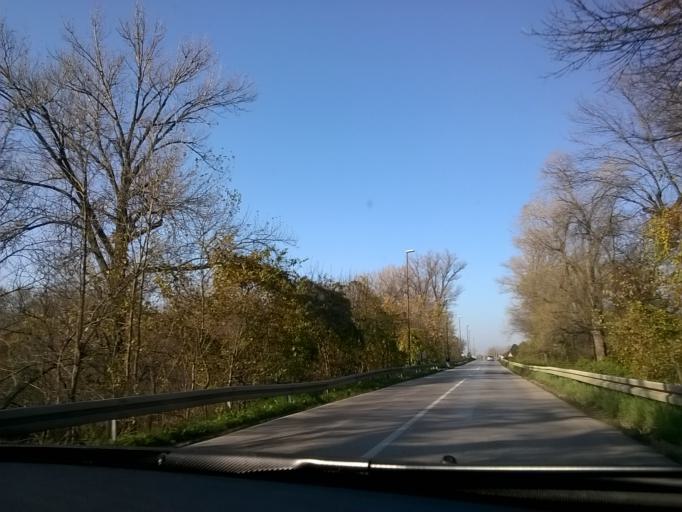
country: RS
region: Autonomna Pokrajina Vojvodina
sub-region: Juznobanatski Okrug
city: Pancevo
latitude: 44.8687
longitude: 20.6241
